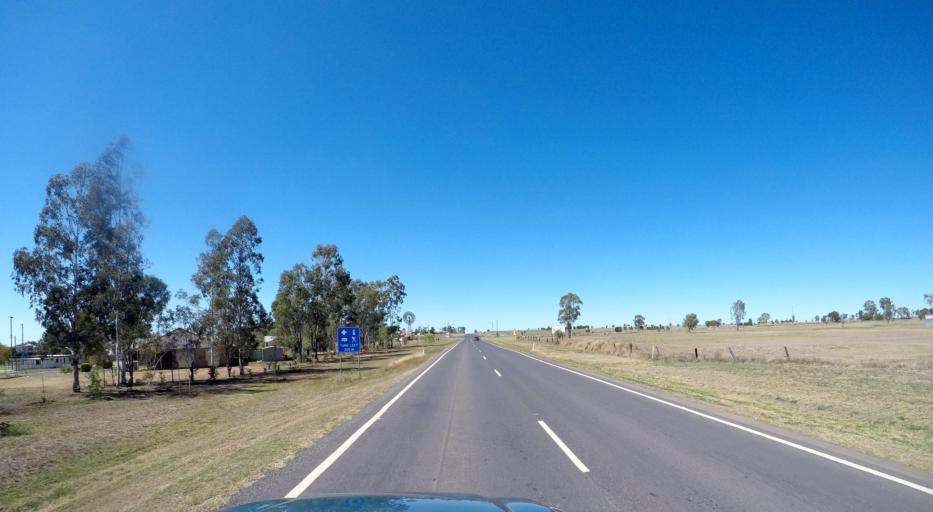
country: AU
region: Queensland
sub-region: Banana
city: Taroom
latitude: -26.1202
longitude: 149.9563
